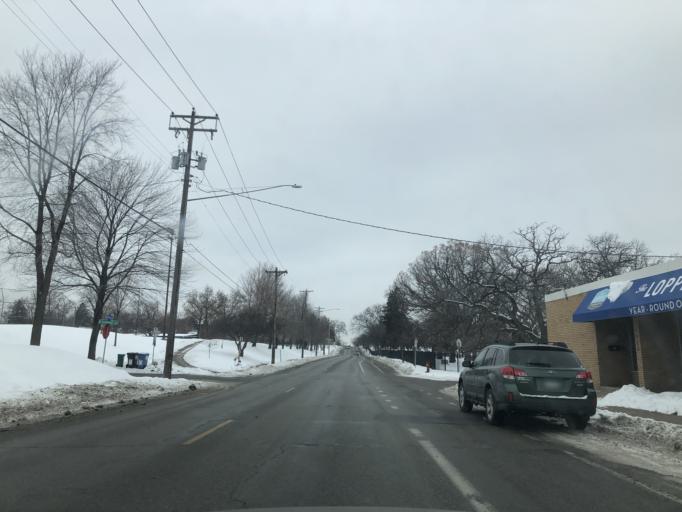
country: US
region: Minnesota
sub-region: Anoka County
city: Columbia Heights
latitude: 45.0240
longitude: -93.2977
